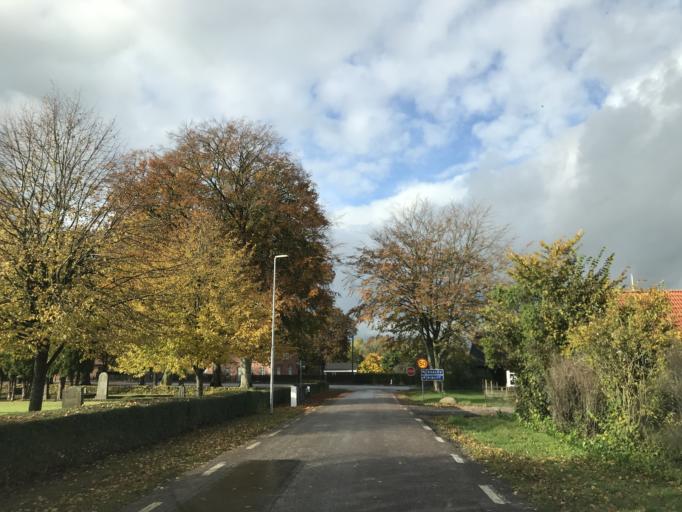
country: SE
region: Skane
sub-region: Svalovs Kommun
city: Svaloev
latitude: 55.9108
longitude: 13.1424
